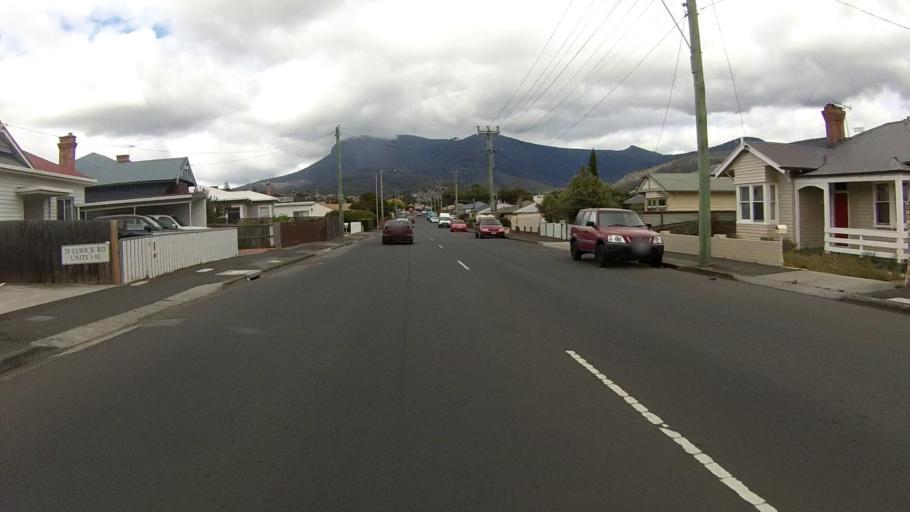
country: AU
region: Tasmania
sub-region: Glenorchy
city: Glenorchy
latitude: -42.8306
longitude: 147.2818
